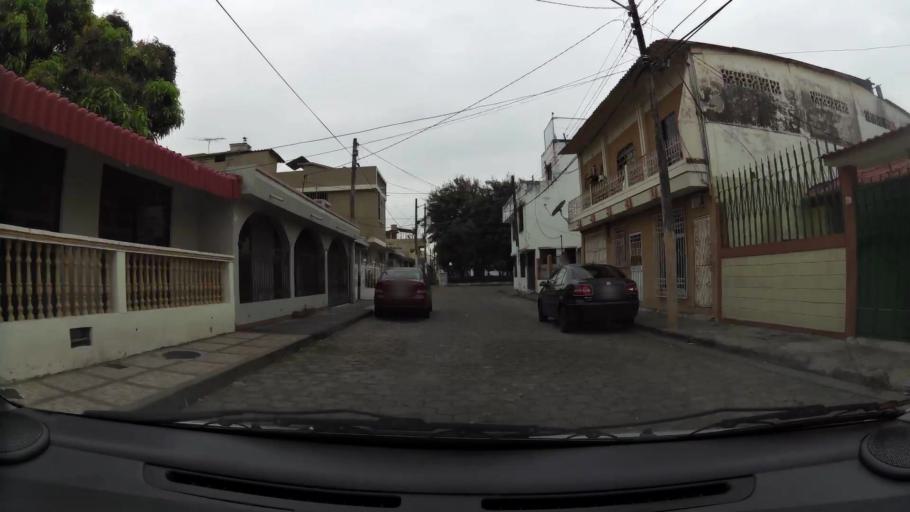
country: EC
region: Guayas
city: Eloy Alfaro
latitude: -2.1373
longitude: -79.9031
